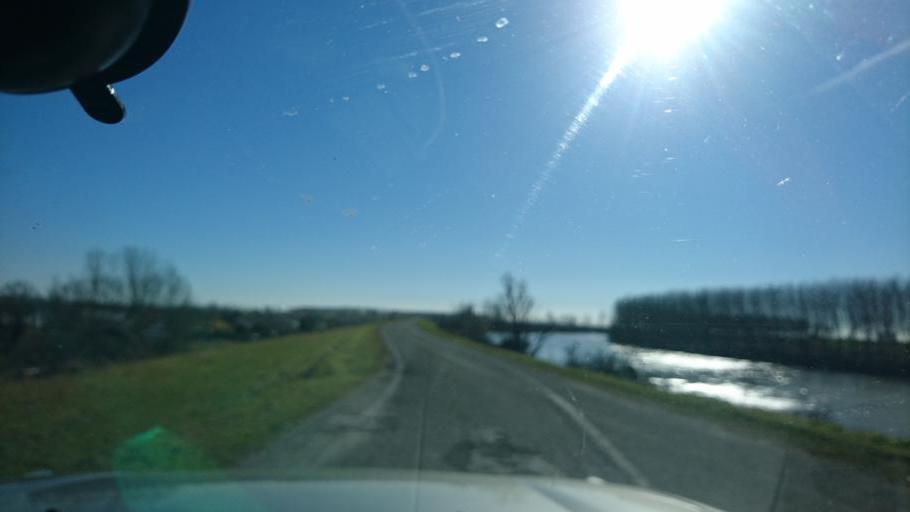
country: IT
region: Veneto
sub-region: Provincia di Rovigo
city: Ariano
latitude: 44.9414
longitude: 12.1271
